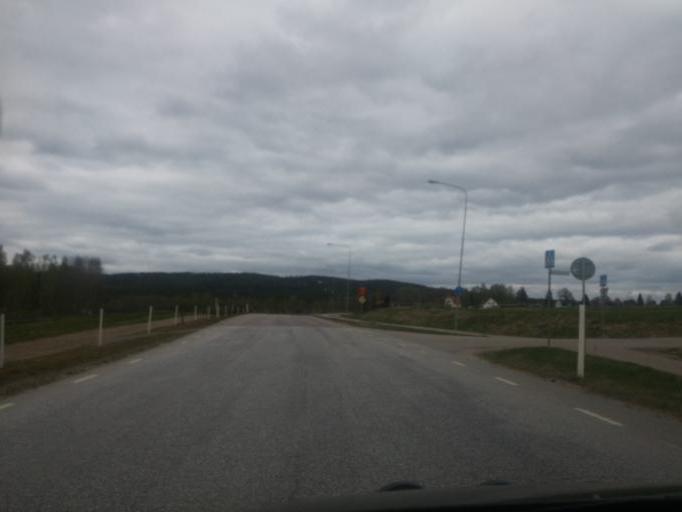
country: SE
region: Gaevleborg
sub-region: Ljusdals Kommun
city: Ljusdal
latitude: 61.8341
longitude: 16.0710
